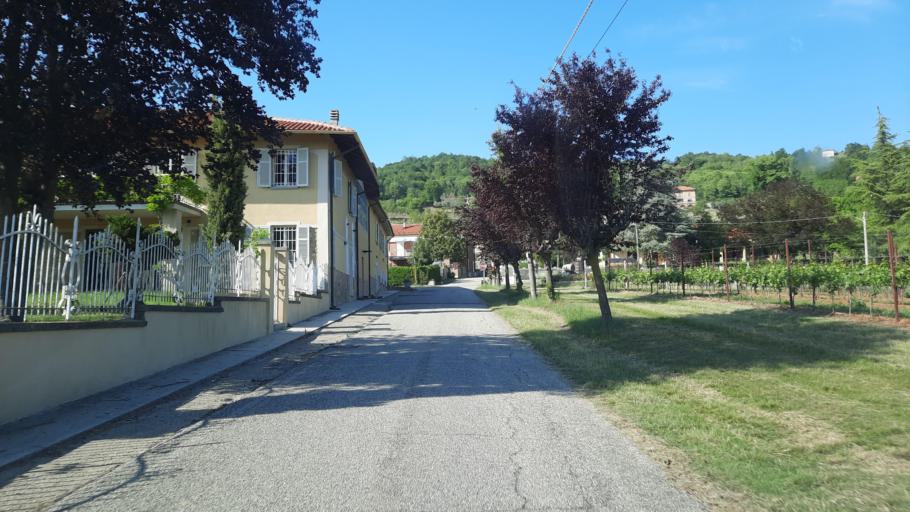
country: IT
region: Piedmont
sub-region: Provincia di Alessandria
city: Alfiano Natta
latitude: 45.0506
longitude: 8.1991
